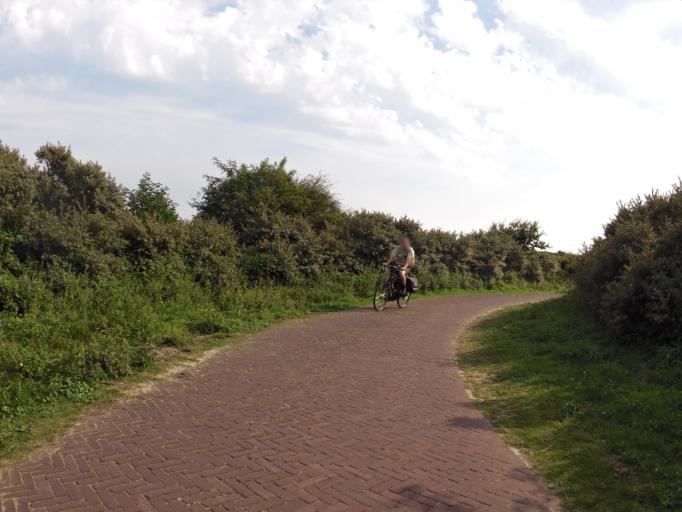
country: NL
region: North Holland
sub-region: Gemeente Bergen
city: Egmond aan Zee
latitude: 52.5945
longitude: 4.6373
